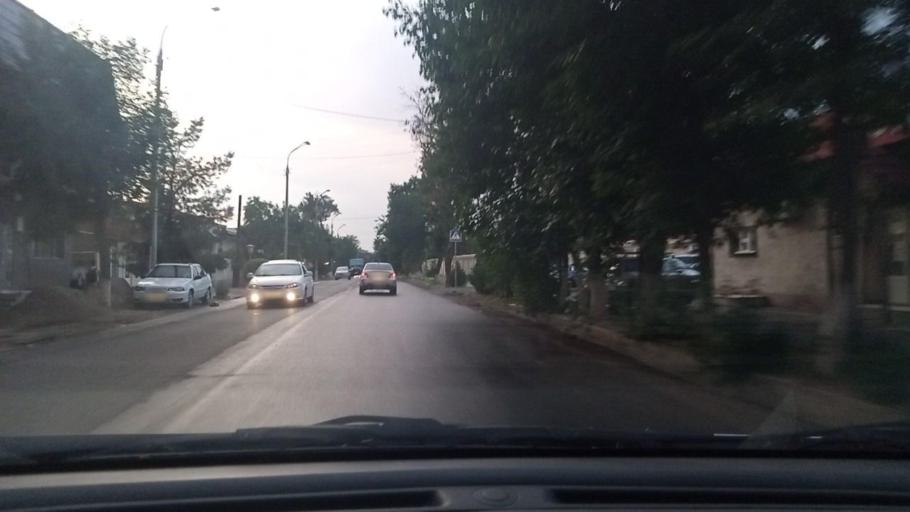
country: UZ
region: Toshkent Shahri
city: Tashkent
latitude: 41.2814
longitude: 69.2856
